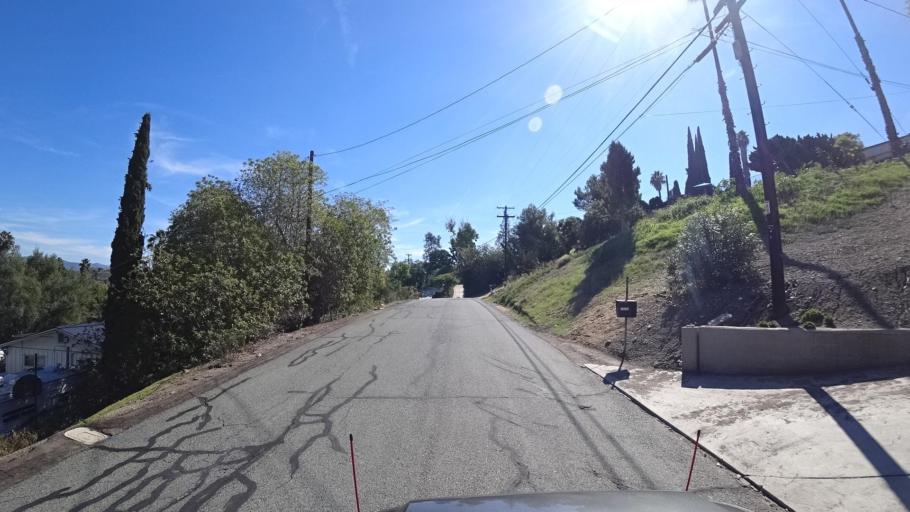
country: US
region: California
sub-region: San Diego County
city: Casa de Oro-Mount Helix
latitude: 32.7509
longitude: -116.9678
